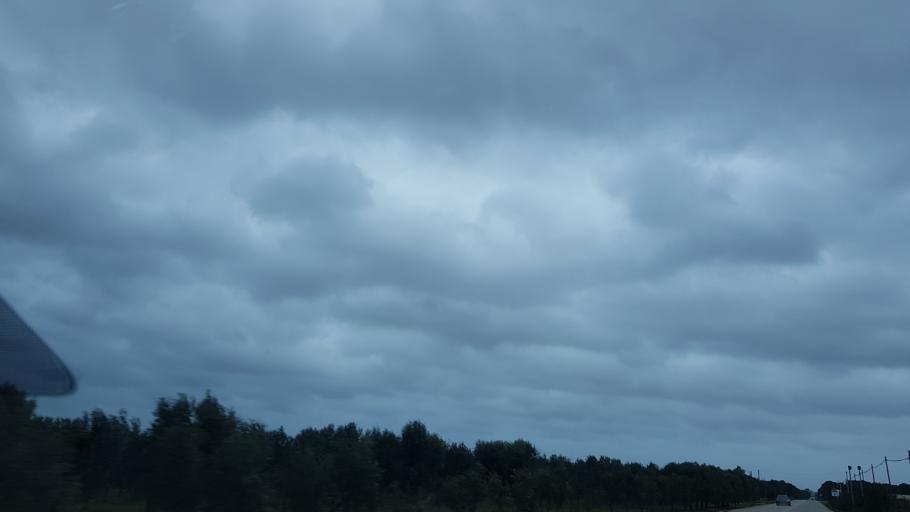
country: IT
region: Apulia
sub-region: Provincia di Brindisi
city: Brindisi
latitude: 40.6498
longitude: 17.8411
